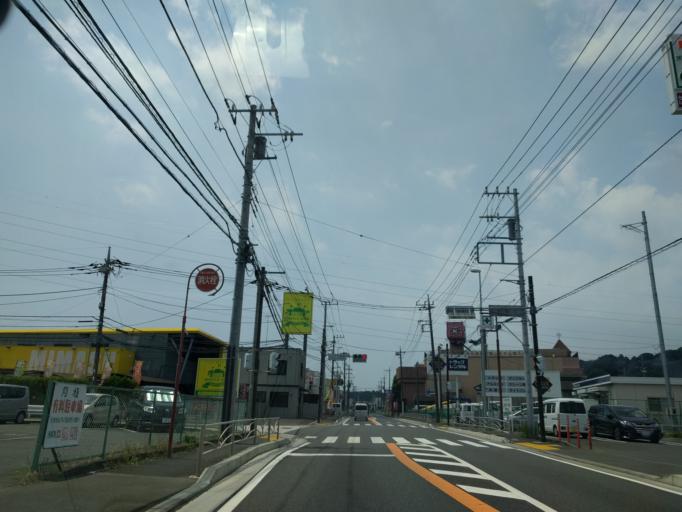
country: JP
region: Kanagawa
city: Minami-rinkan
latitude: 35.4943
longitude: 139.5074
